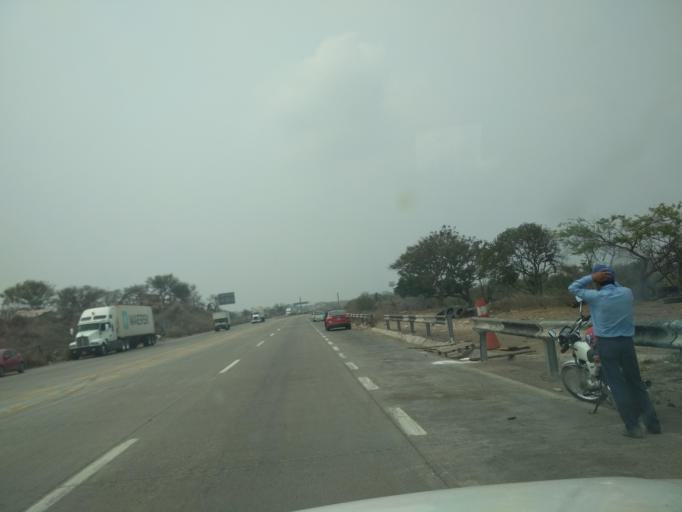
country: MX
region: Veracruz
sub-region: Veracruz
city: Fraccionamiento Geovillas los Pinos
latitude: 19.2150
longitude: -96.2210
